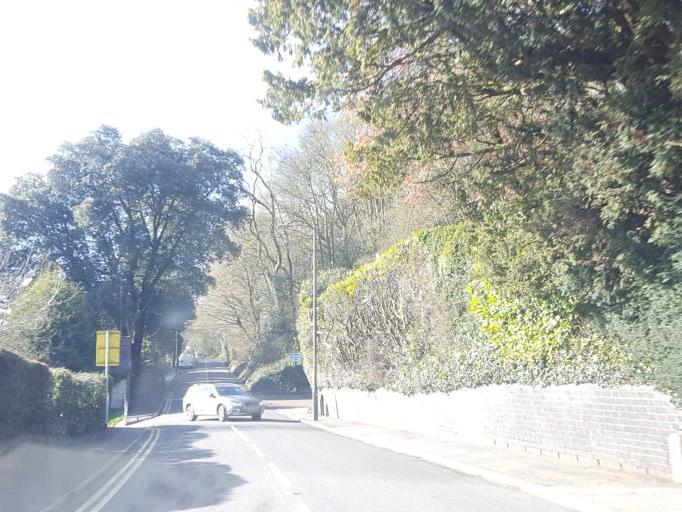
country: GB
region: England
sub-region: Worcestershire
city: Great Malvern
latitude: 52.0714
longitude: -2.3339
